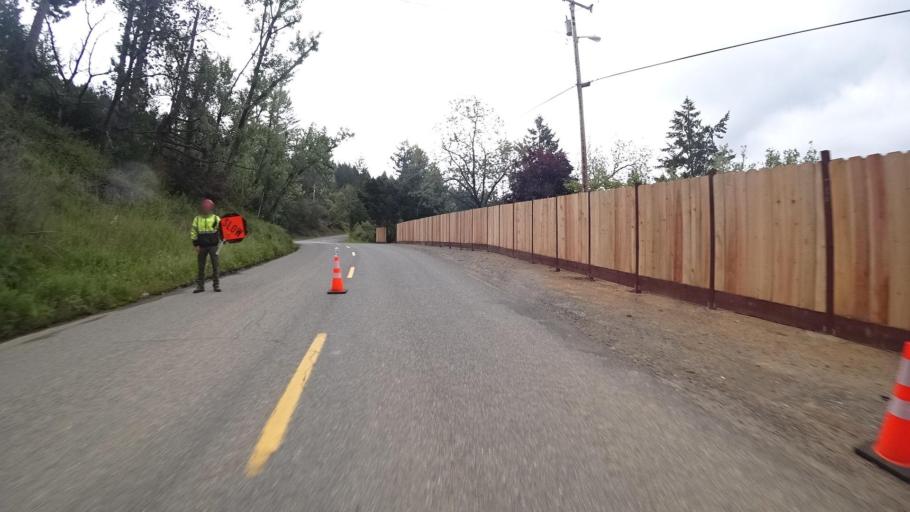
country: US
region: California
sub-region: Humboldt County
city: Redway
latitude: 40.2956
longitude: -123.8272
